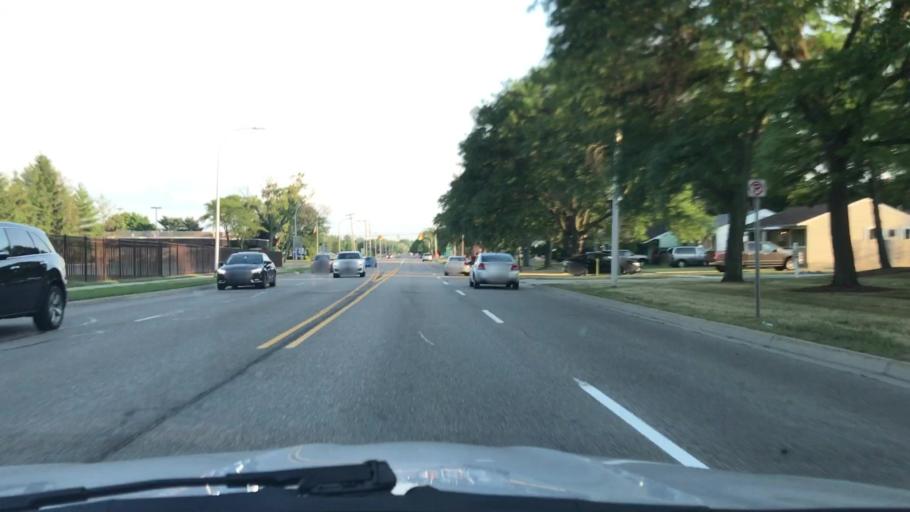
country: US
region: Michigan
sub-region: Oakland County
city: Clawson
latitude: 42.5274
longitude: -83.1653
